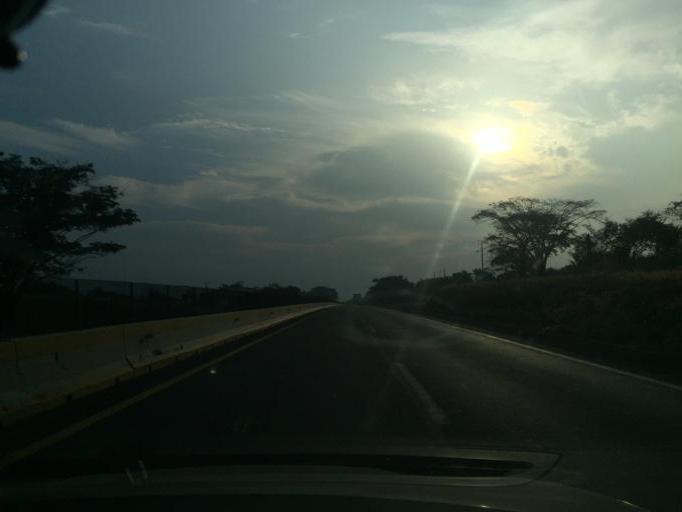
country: MX
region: Veracruz
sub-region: Omealca
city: Mata Tenatito (Casco Hacienda)
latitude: 18.7911
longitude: -96.5682
